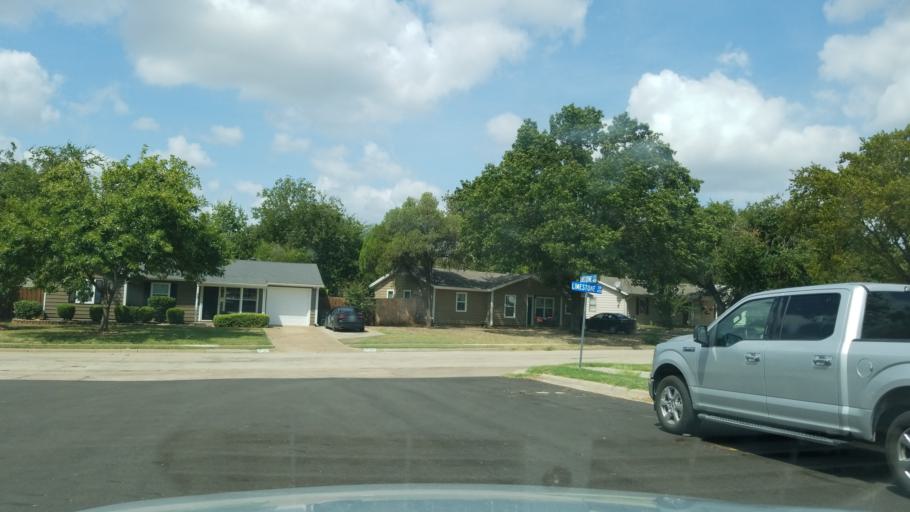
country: US
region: Texas
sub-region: Tarrant County
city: Euless
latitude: 32.8414
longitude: -97.0876
